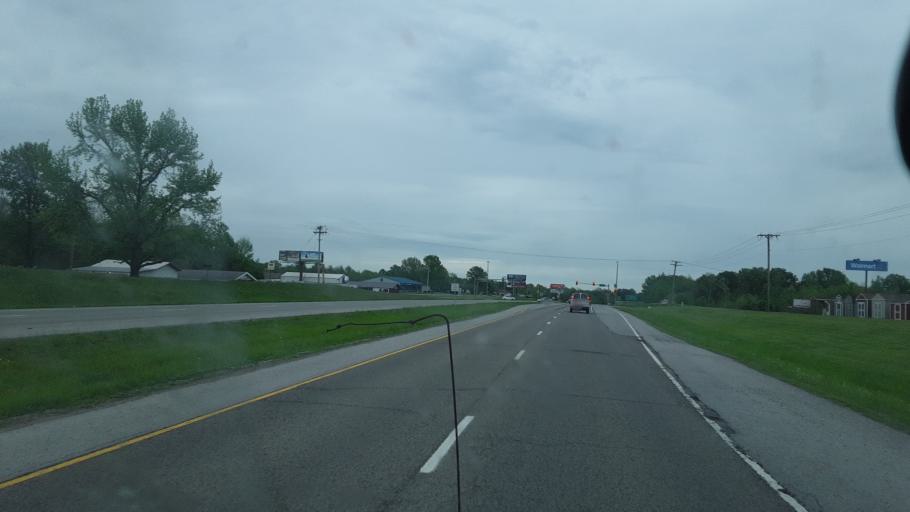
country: US
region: Illinois
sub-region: Jackson County
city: Murphysboro
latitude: 37.7623
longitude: -89.2829
